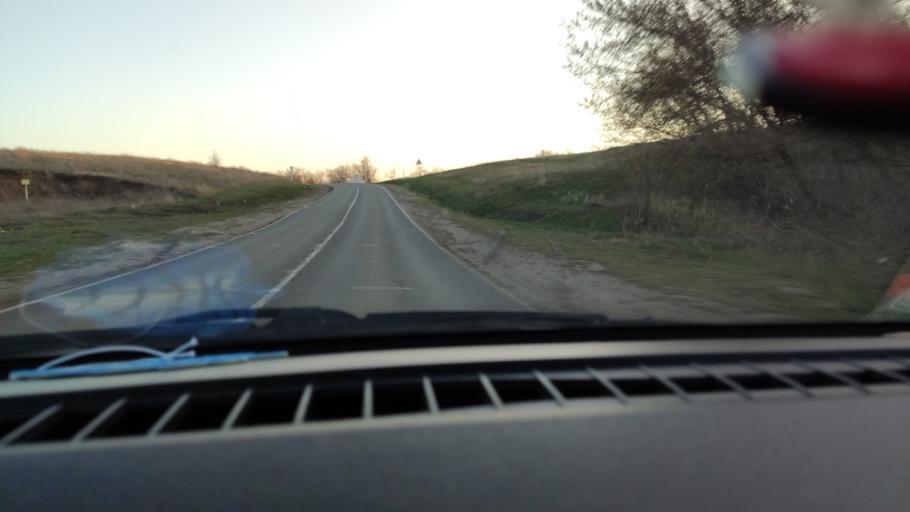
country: RU
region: Saratov
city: Privolzhskiy
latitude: 51.3287
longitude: 46.0334
